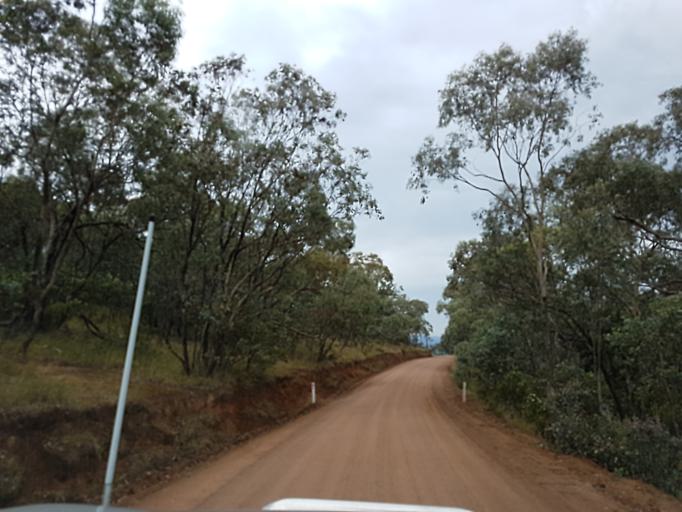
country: AU
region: New South Wales
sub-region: Snowy River
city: Jindabyne
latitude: -36.9348
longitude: 148.3507
